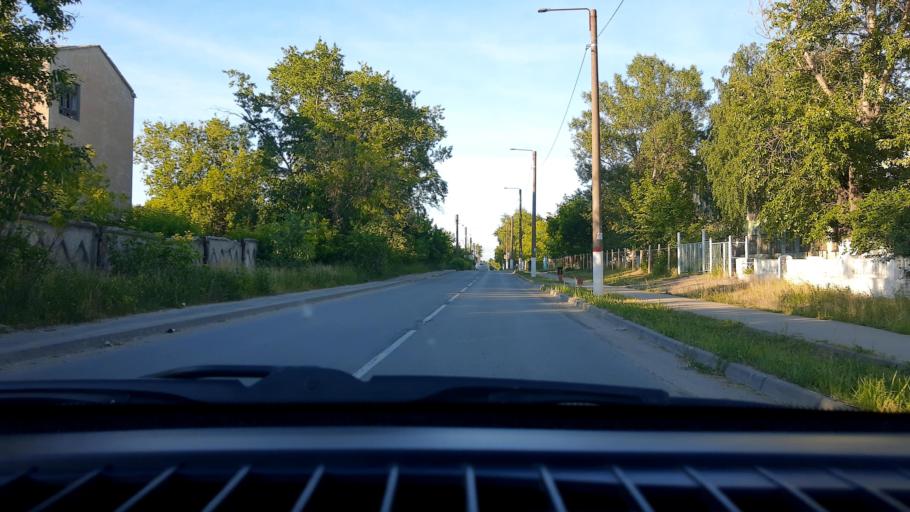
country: RU
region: Nizjnij Novgorod
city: Dzerzhinsk
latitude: 56.2426
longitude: 43.4863
